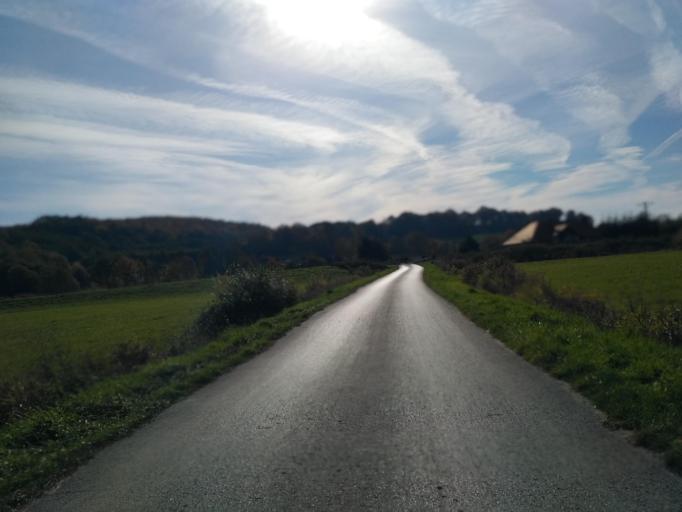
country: PL
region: Subcarpathian Voivodeship
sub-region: Powiat ropczycko-sedziszowski
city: Iwierzyce
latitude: 50.0488
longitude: 21.7497
